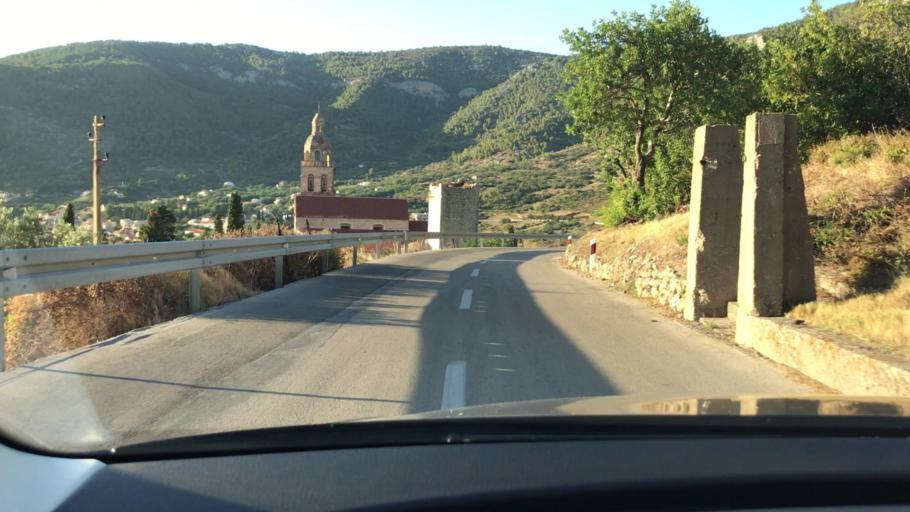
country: HR
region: Splitsko-Dalmatinska
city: Komiza
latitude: 43.0397
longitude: 16.0966
